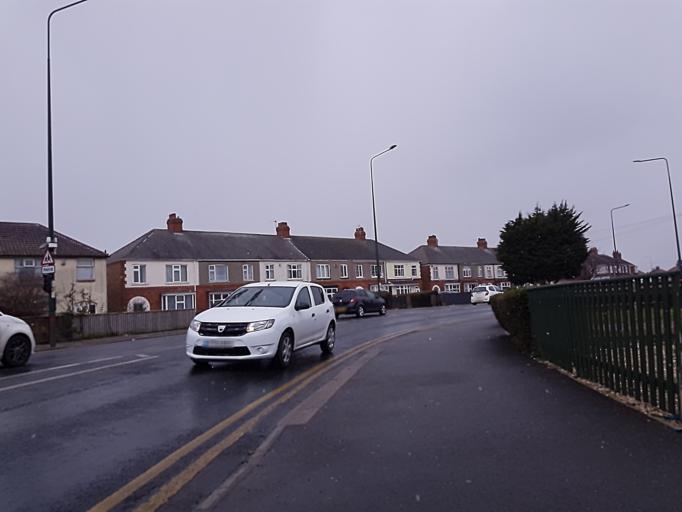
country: GB
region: England
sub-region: North East Lincolnshire
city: Grimbsy
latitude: 53.5621
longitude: -0.1138
